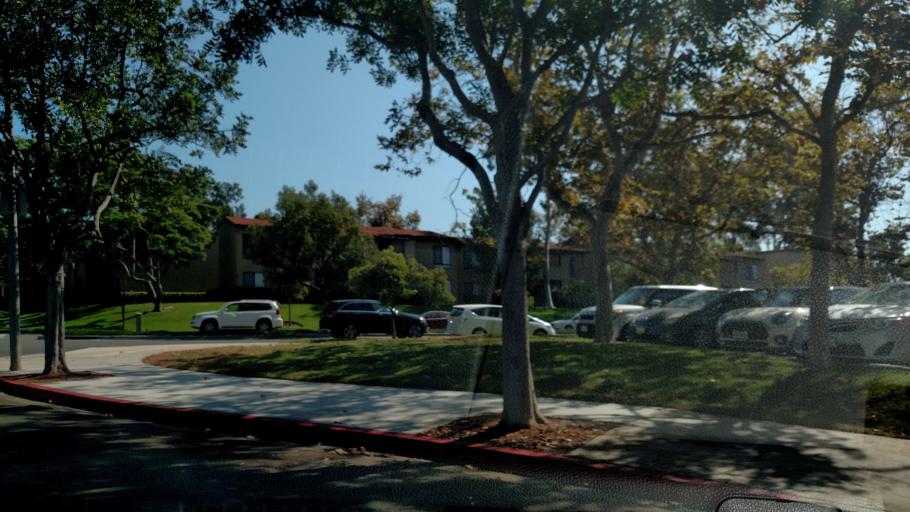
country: US
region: California
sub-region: Orange County
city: Irvine
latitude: 33.6706
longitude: -117.8309
